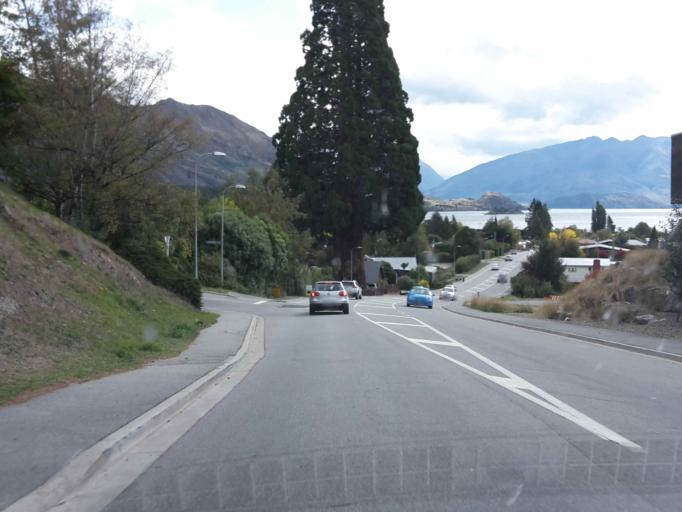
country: NZ
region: Otago
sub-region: Queenstown-Lakes District
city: Wanaka
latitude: -44.7048
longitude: 169.1344
